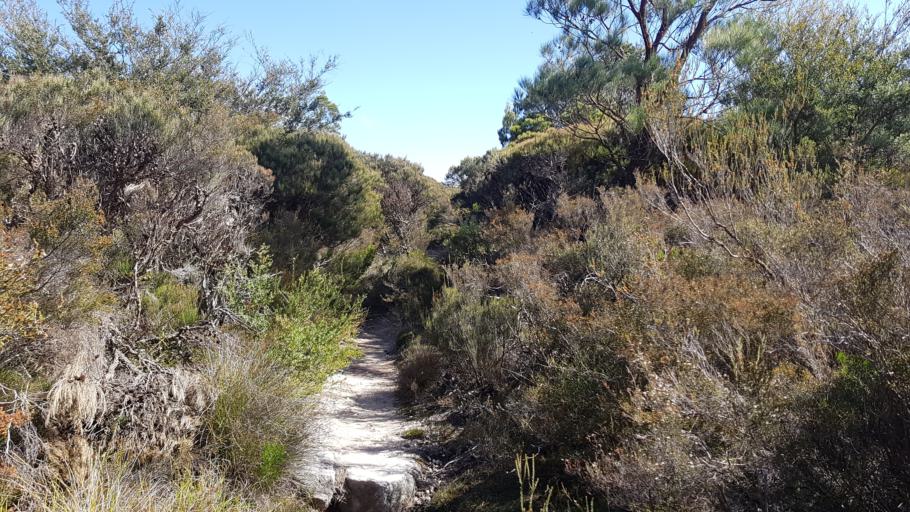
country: AU
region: New South Wales
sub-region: Blue Mountains Municipality
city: Katoomba
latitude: -33.9855
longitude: 150.1206
